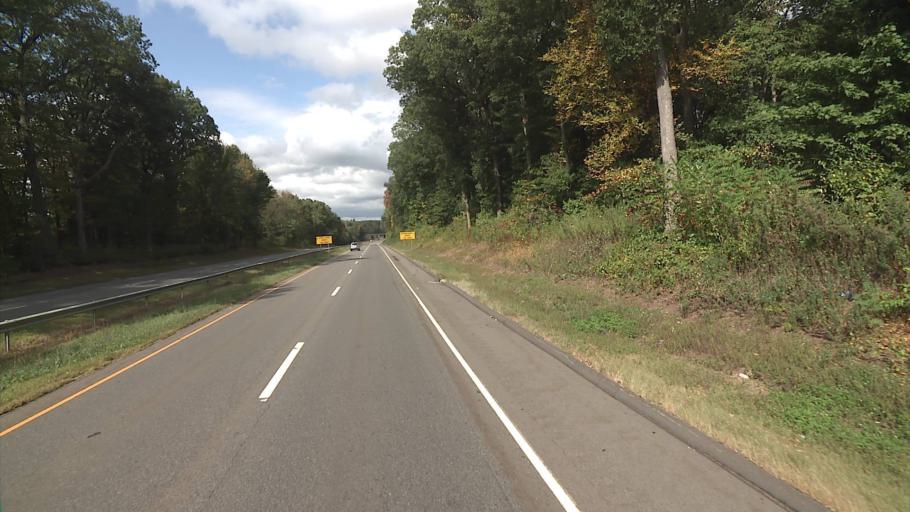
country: US
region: Connecticut
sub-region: New Haven County
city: Meriden
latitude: 41.5533
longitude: -72.7745
